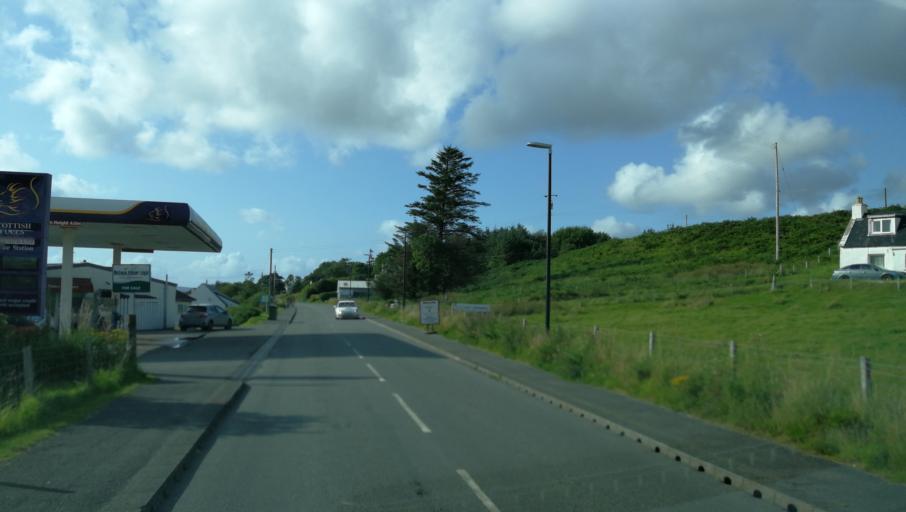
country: GB
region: Scotland
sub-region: Highland
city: Isle of Skye
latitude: 57.4330
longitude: -6.5749
